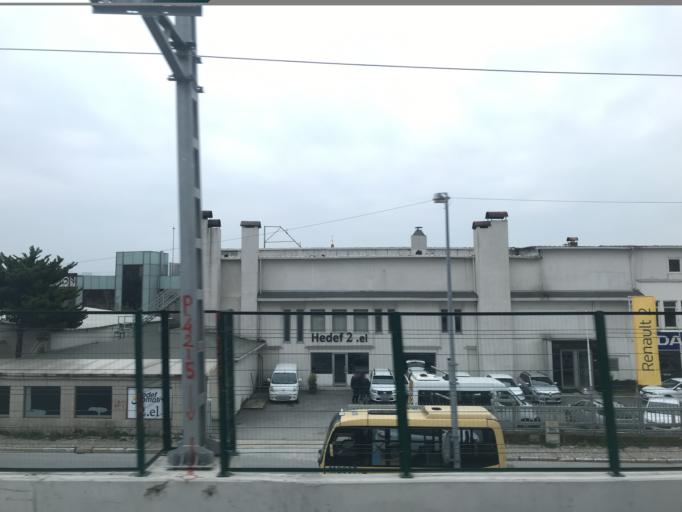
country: TR
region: Istanbul
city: Zeytinburnu
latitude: 40.9824
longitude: 28.8906
